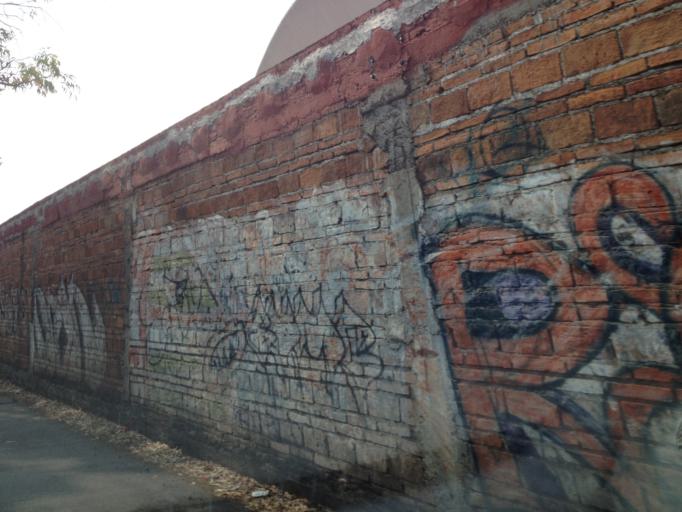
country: MX
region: Michoacan
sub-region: Morelia
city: Morelos
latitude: 19.6717
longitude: -101.2242
